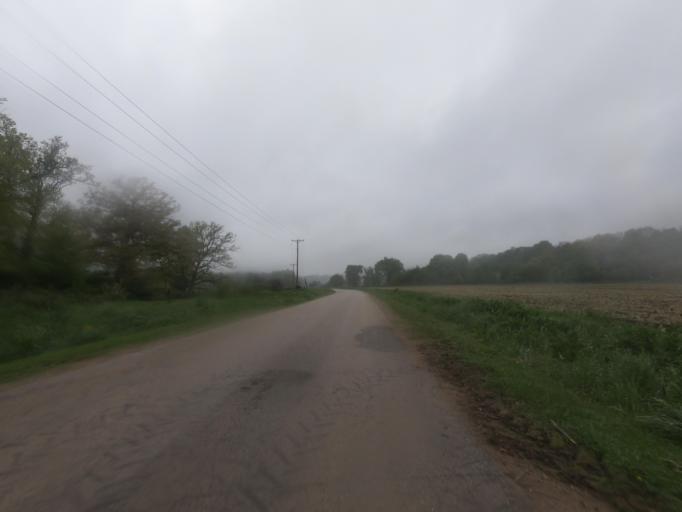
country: US
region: Wisconsin
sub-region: Grant County
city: Hazel Green
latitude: 42.5093
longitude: -90.4711
